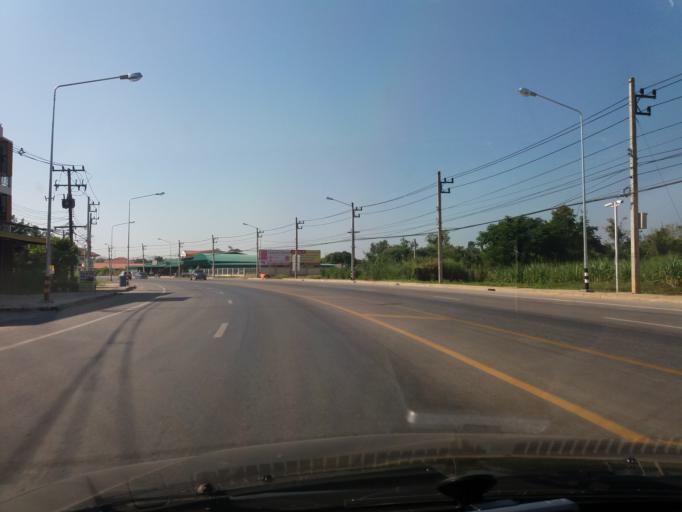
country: TH
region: Kamphaeng Phet
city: Khlong Khlung
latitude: 16.2216
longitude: 99.7282
